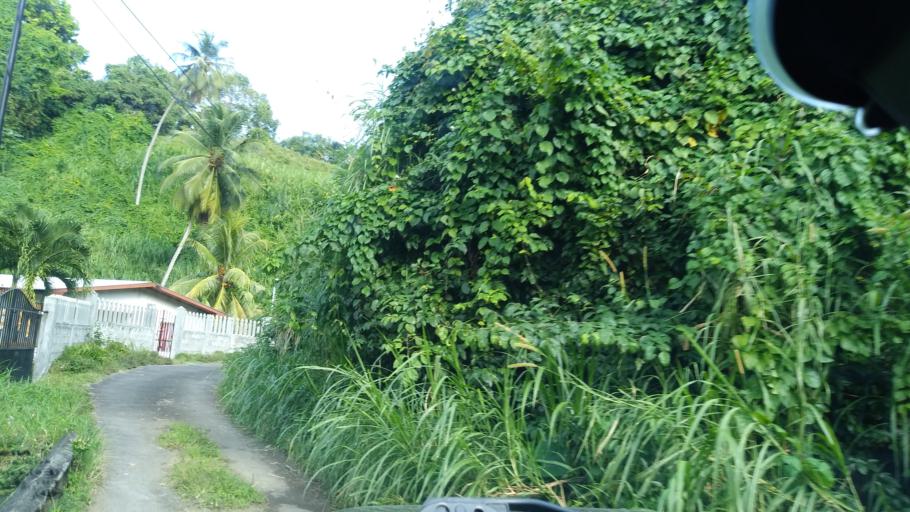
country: VC
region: Charlotte
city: Byera Village
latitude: 13.2384
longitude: -61.1332
